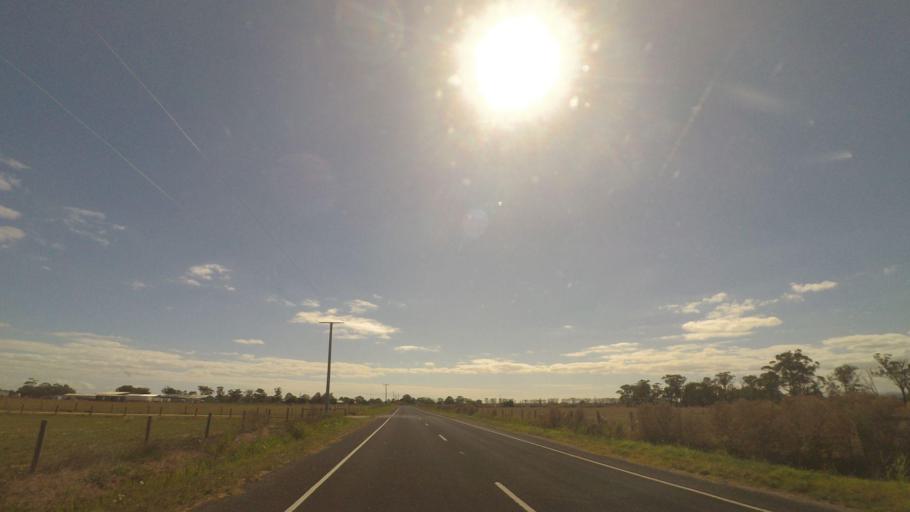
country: AU
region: Victoria
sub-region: Cardinia
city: Pakenham South
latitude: -38.1544
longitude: 145.4913
